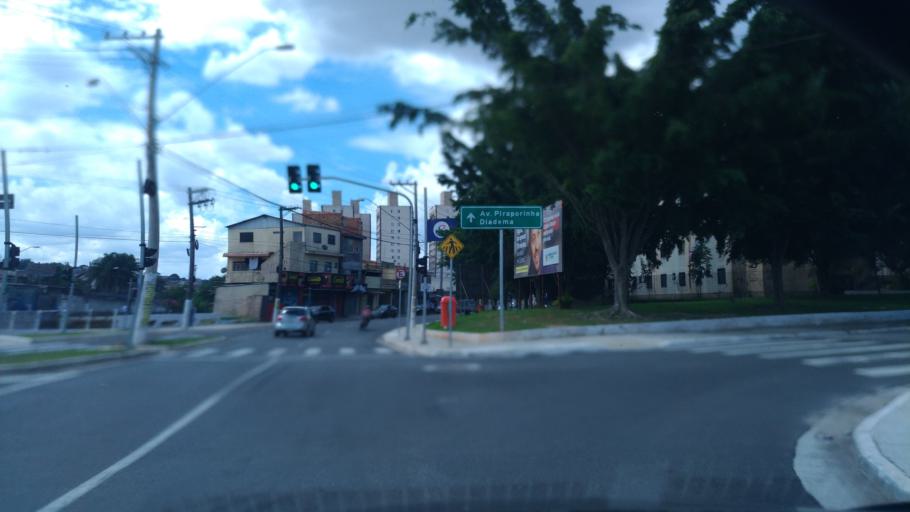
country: BR
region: Sao Paulo
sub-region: Sao Bernardo Do Campo
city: Sao Bernardo do Campo
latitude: -23.7078
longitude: -46.5886
